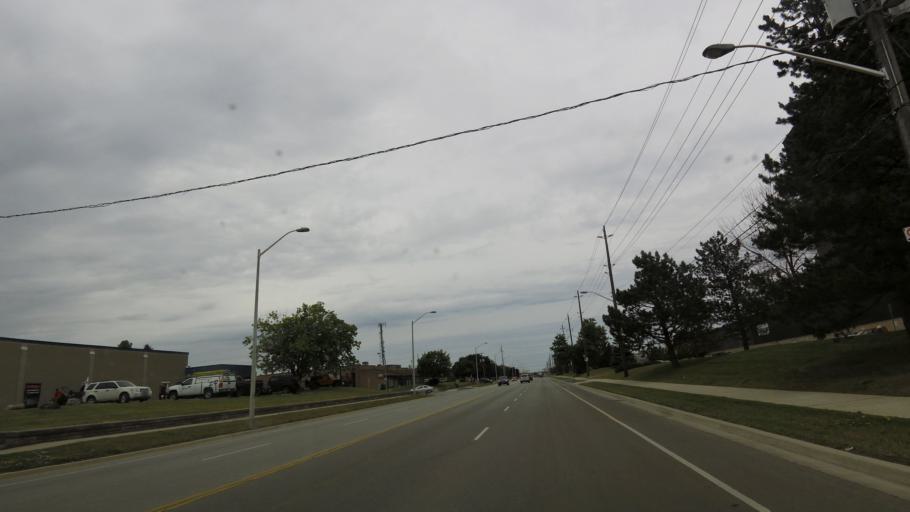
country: CA
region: Ontario
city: Burlington
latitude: 43.3873
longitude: -79.7570
